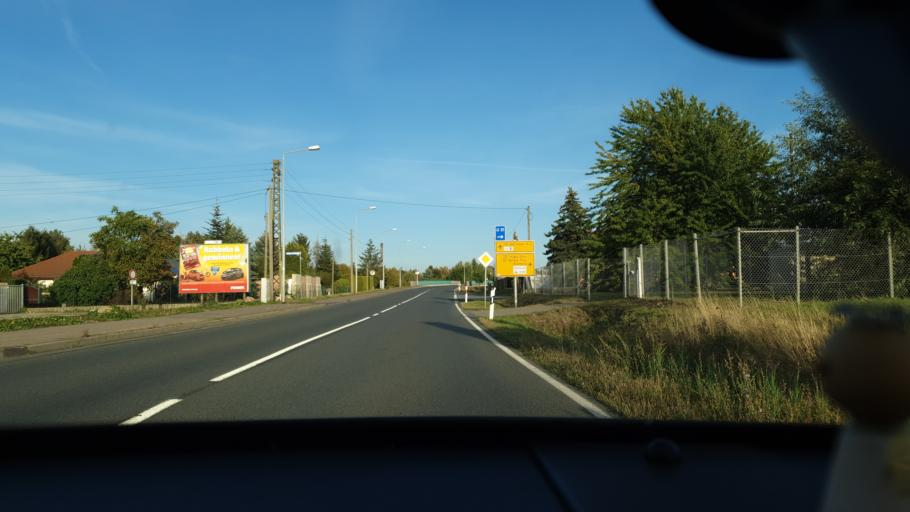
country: DE
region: Saxony
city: Eilenburg
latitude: 51.4587
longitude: 12.6083
